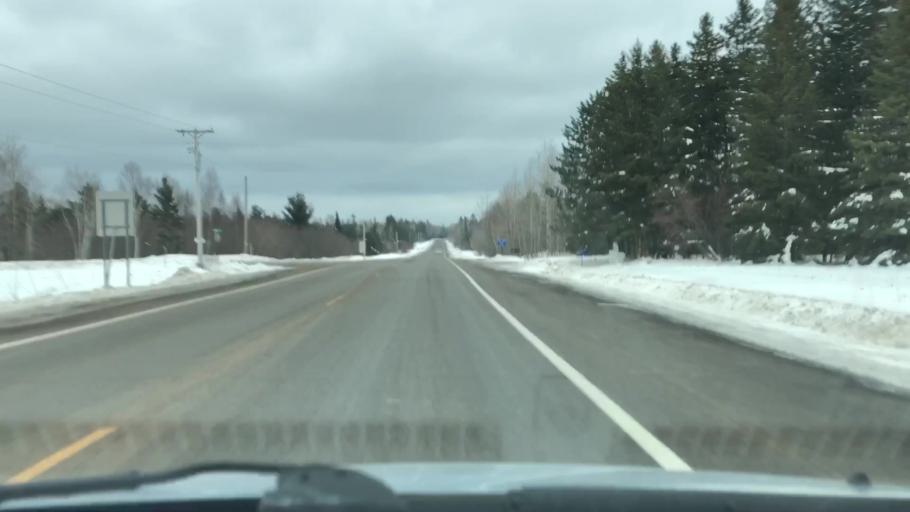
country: US
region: Minnesota
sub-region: Carlton County
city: Esko
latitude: 46.6929
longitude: -92.3649
